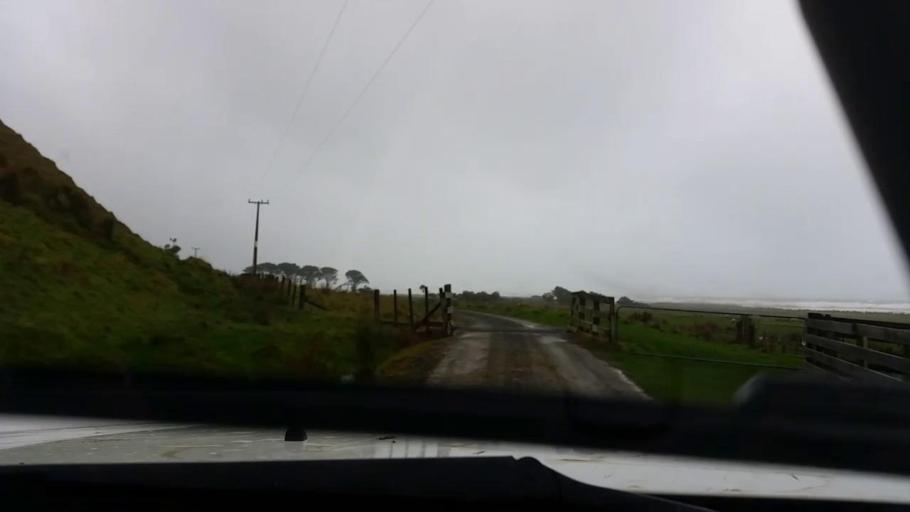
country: NZ
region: Wellington
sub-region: Masterton District
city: Masterton
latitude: -41.2645
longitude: 175.8907
